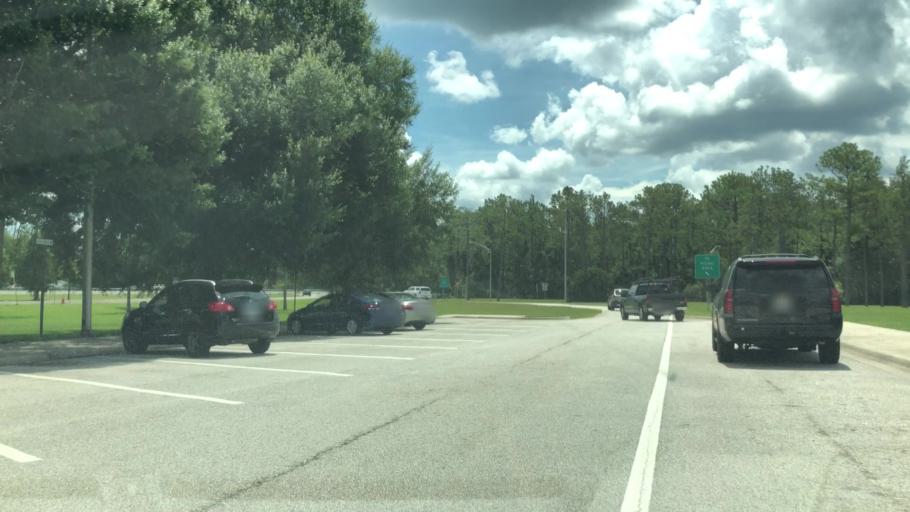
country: US
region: Florida
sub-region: Saint Johns County
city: Saint Augustine Shores
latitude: 29.7152
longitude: -81.3347
